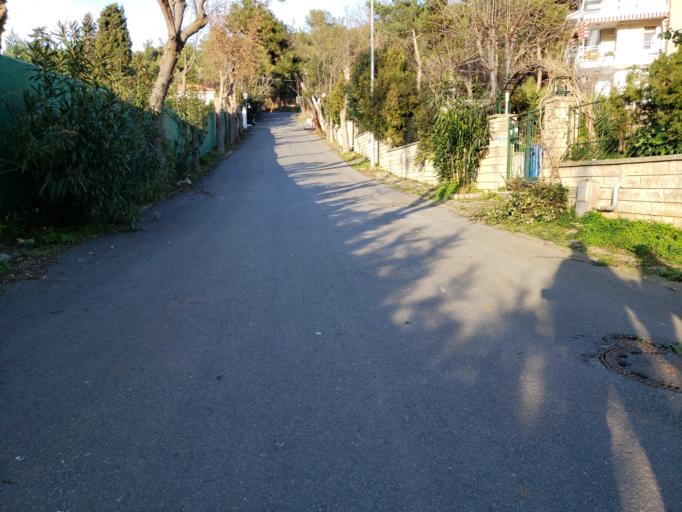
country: TR
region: Istanbul
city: Adalan
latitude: 40.8806
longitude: 29.0914
